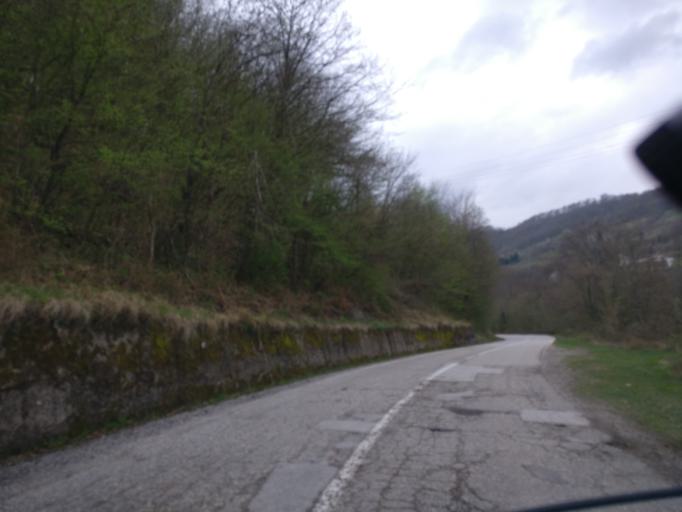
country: BA
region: Republika Srpska
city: Foca
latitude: 43.4693
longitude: 18.7487
